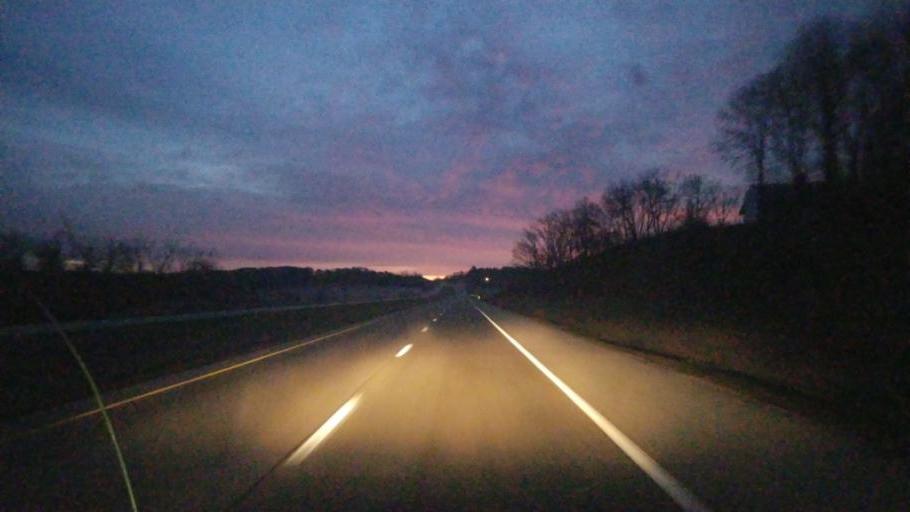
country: US
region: Missouri
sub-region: Howell County
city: Mountain View
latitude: 36.9890
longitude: -91.5348
